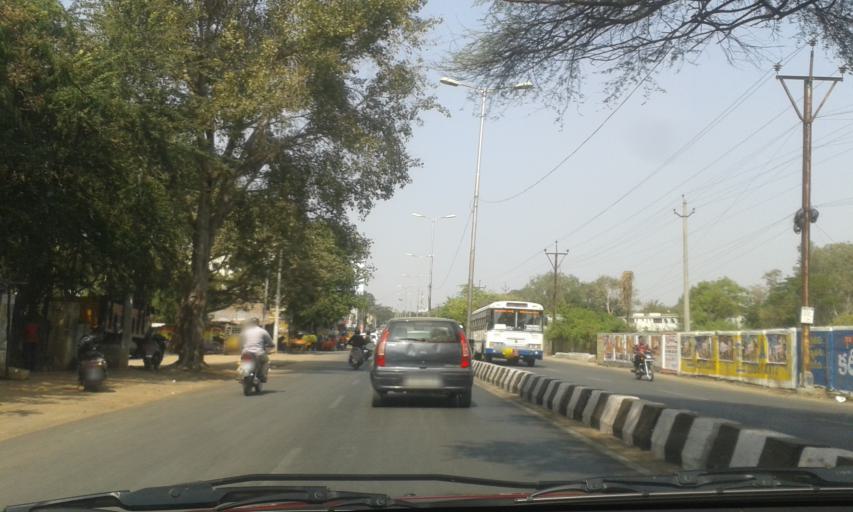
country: IN
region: Telangana
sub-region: Rangareddi
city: Secunderabad
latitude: 17.4971
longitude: 78.5132
